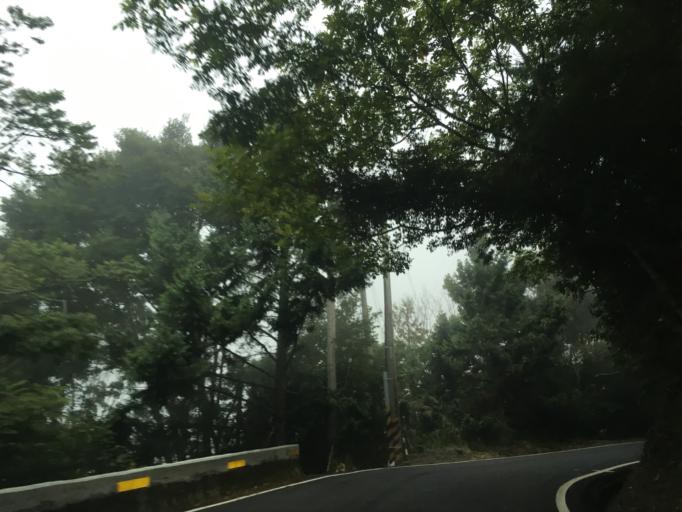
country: TW
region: Taiwan
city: Fengyuan
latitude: 24.2458
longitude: 120.9351
